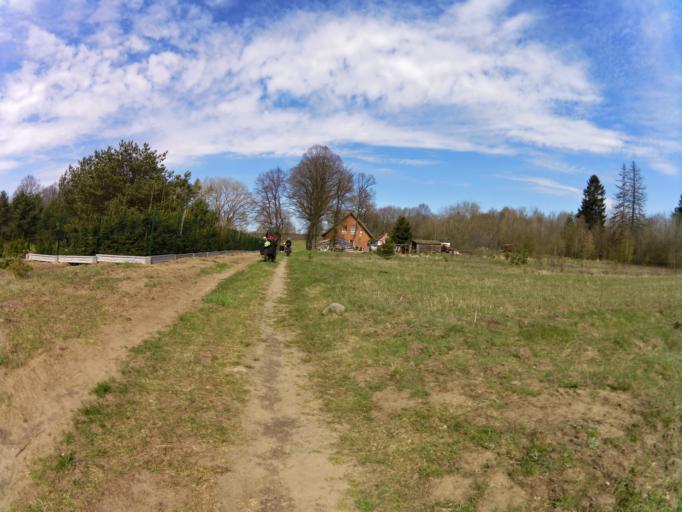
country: PL
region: West Pomeranian Voivodeship
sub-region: Powiat szczecinecki
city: Szczecinek
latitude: 53.7773
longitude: 16.6274
